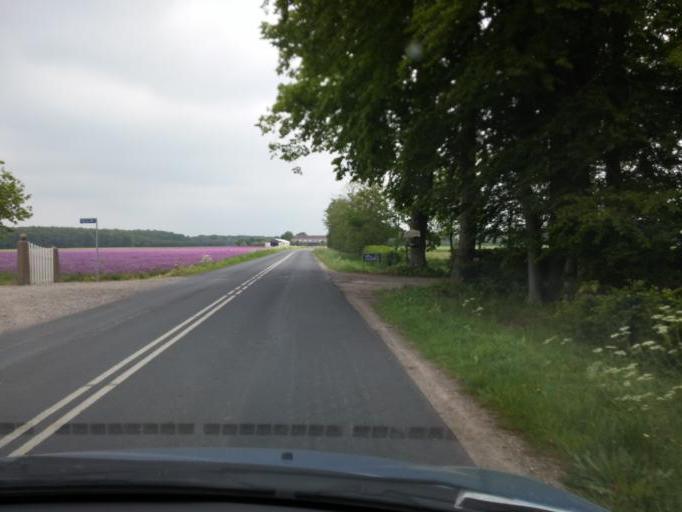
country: DK
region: South Denmark
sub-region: Kerteminde Kommune
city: Kerteminde
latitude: 55.4167
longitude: 10.6051
